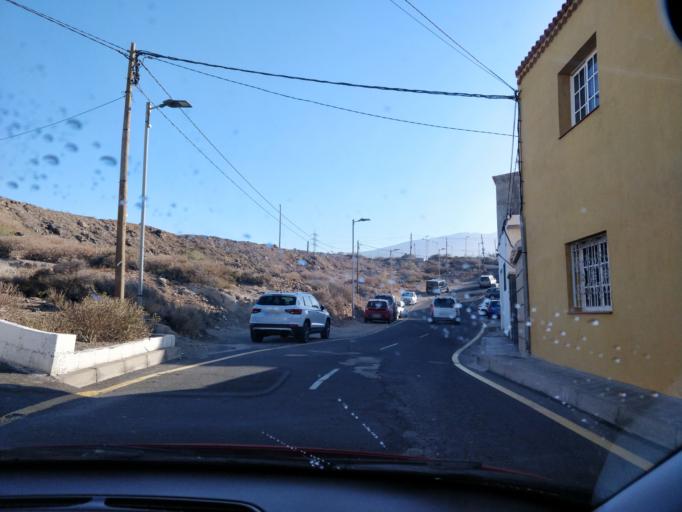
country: ES
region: Canary Islands
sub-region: Provincia de Santa Cruz de Tenerife
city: Candelaria
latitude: 28.3504
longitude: -16.3703
